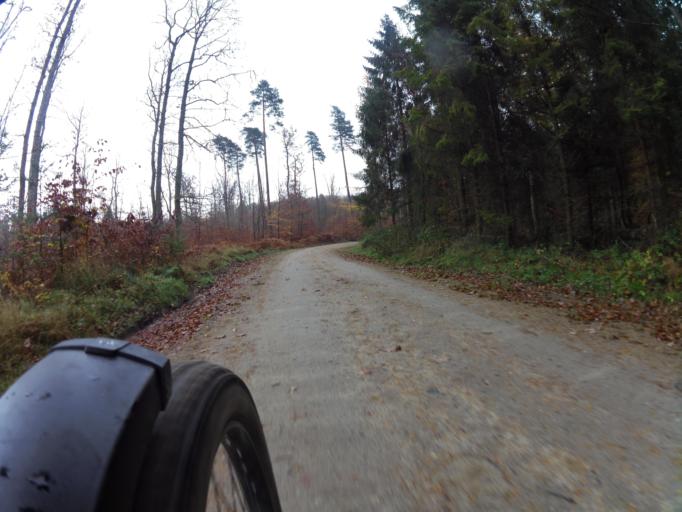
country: PL
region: Pomeranian Voivodeship
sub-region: Powiat pucki
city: Krokowa
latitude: 54.7686
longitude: 18.0950
